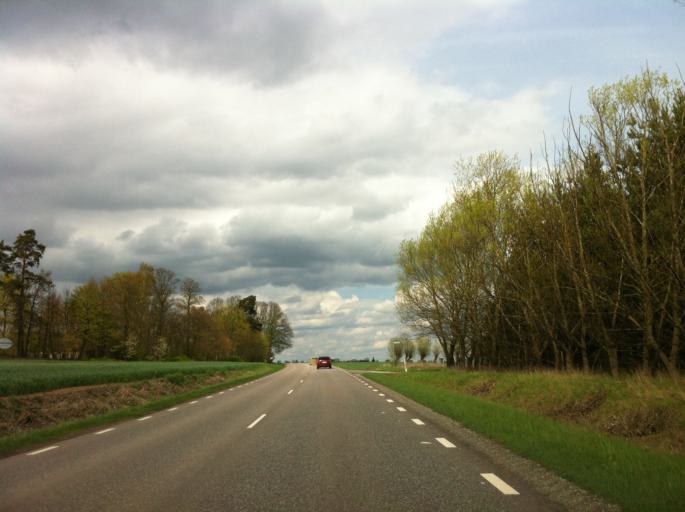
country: SE
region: Skane
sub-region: Kavlinge Kommun
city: Kaevlinge
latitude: 55.8258
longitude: 13.0926
